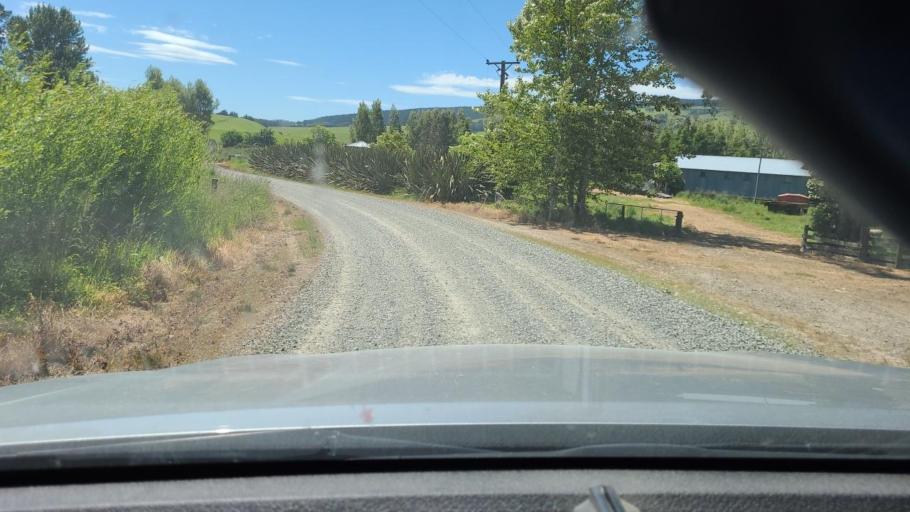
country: NZ
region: Southland
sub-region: Southland District
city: Riverton
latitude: -46.0618
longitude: 167.8524
